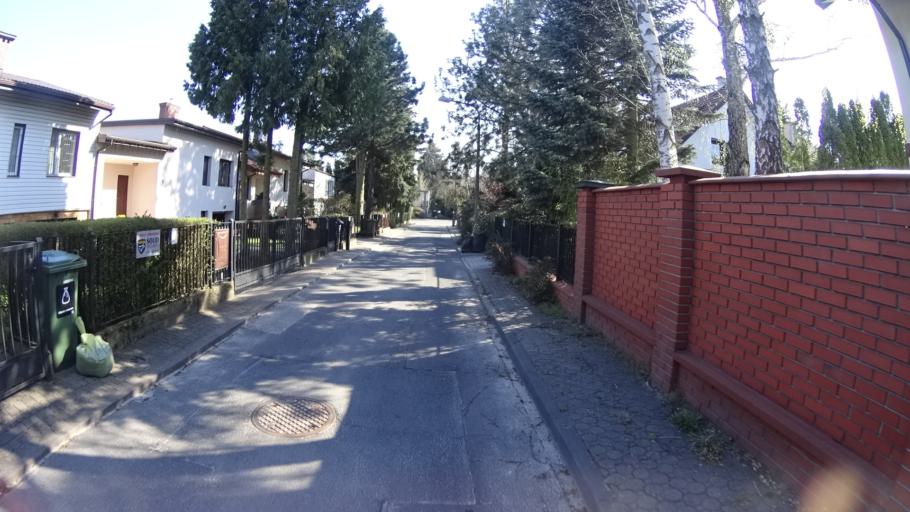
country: PL
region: Masovian Voivodeship
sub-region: Powiat warszawski zachodni
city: Babice
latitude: 52.2517
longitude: 20.8733
